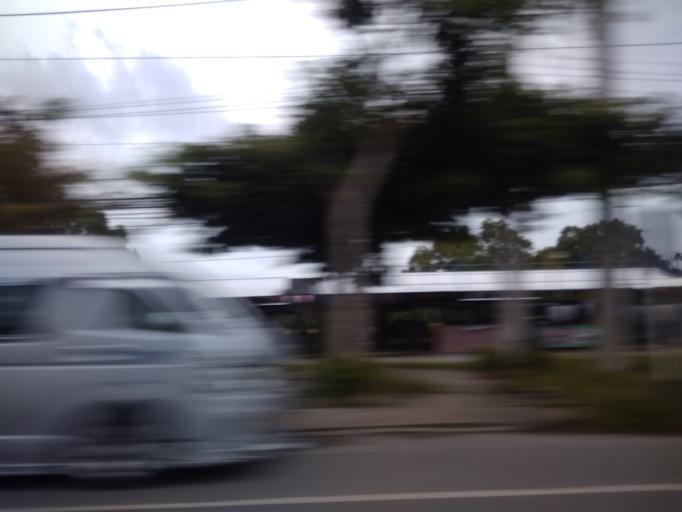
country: TH
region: Phuket
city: Mueang Phuket
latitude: 7.8578
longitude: 98.3804
